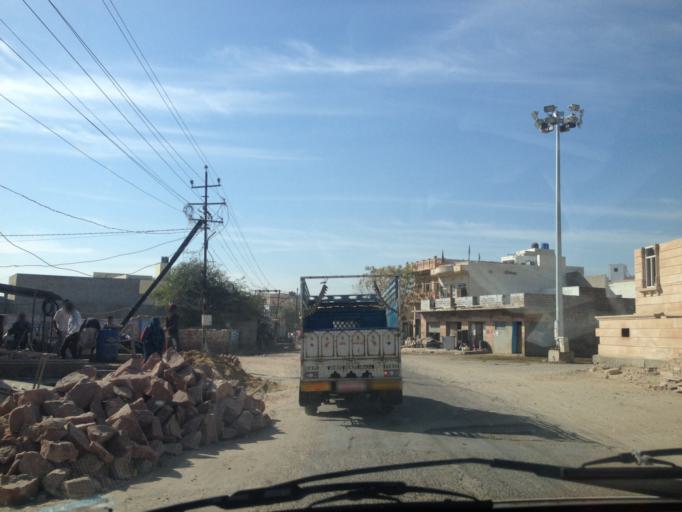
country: IN
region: Rajasthan
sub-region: Nagaur
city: Merta
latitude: 26.6457
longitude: 74.0270
